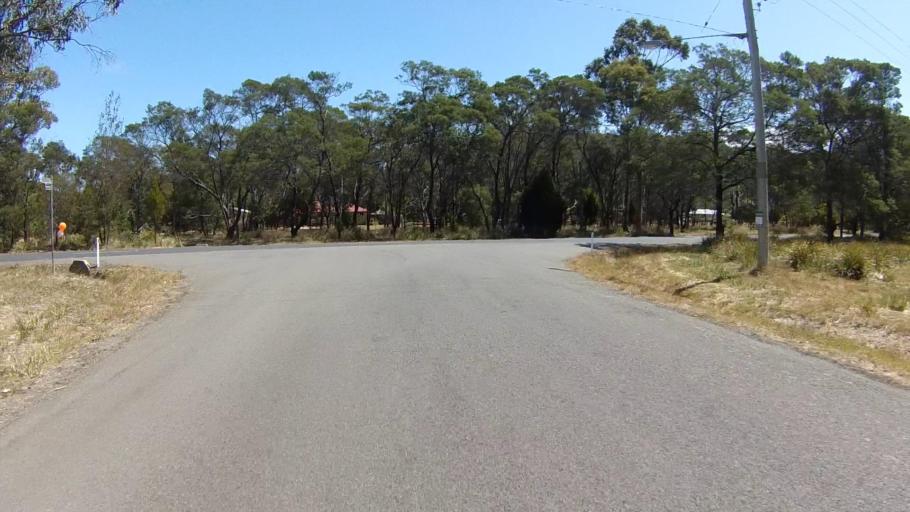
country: AU
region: Tasmania
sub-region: Clarence
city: Sandford
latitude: -42.9646
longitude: 147.4756
